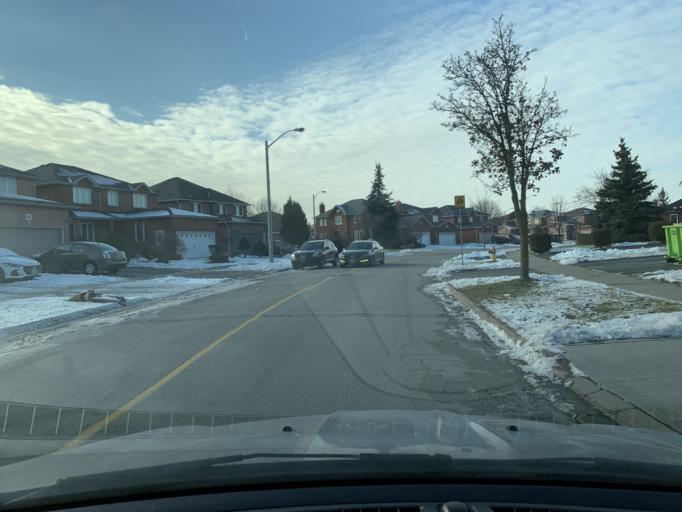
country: CA
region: Ontario
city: Etobicoke
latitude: 43.7207
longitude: -79.6177
